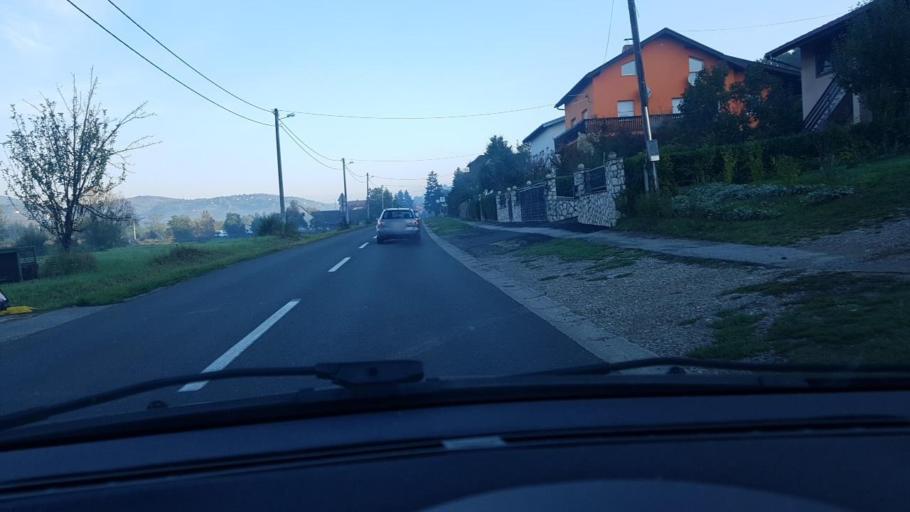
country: HR
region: Grad Zagreb
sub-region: Sesvete
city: Sesvete
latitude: 45.8640
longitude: 16.1150
